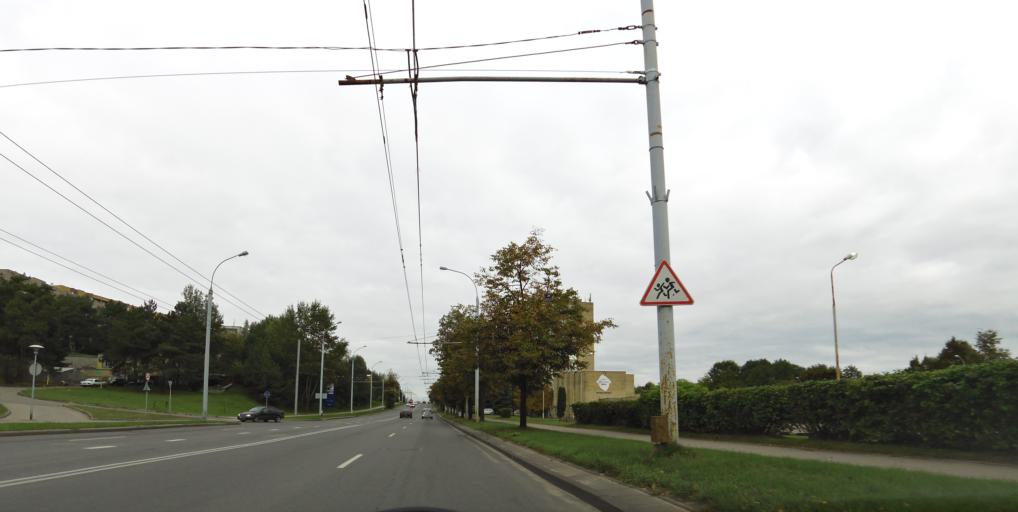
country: LT
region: Vilnius County
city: Rasos
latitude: 54.7066
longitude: 25.3046
